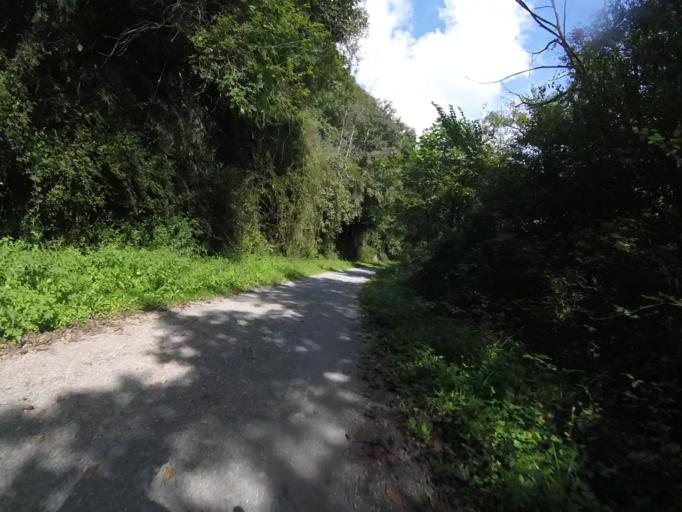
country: ES
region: Navarre
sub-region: Provincia de Navarra
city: Bera
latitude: 43.2639
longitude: -1.6875
